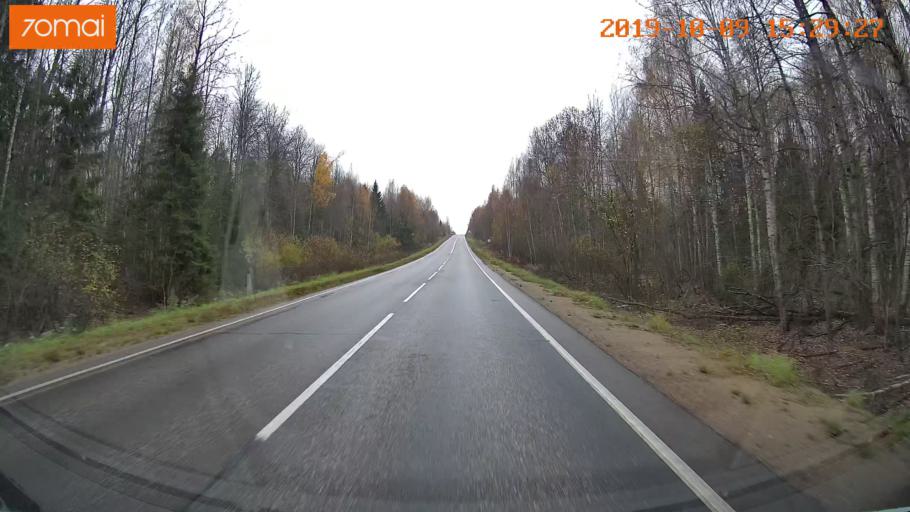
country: RU
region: Kostroma
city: Susanino
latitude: 57.9912
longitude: 41.3425
